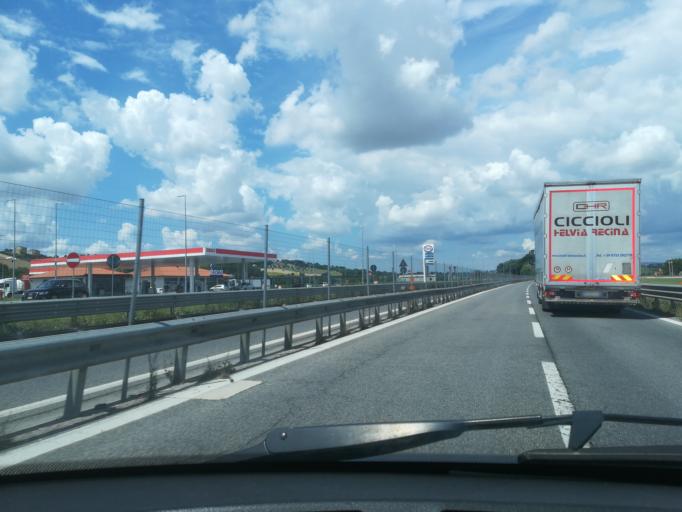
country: IT
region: The Marches
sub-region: Provincia di Macerata
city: Villa San Filippo
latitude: 43.2627
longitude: 13.5636
